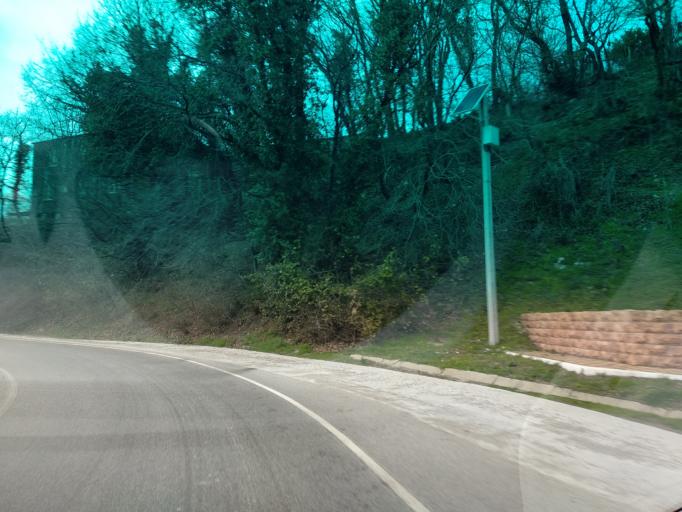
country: RU
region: Krasnodarskiy
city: Tuapse
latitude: 44.0914
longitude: 39.1186
